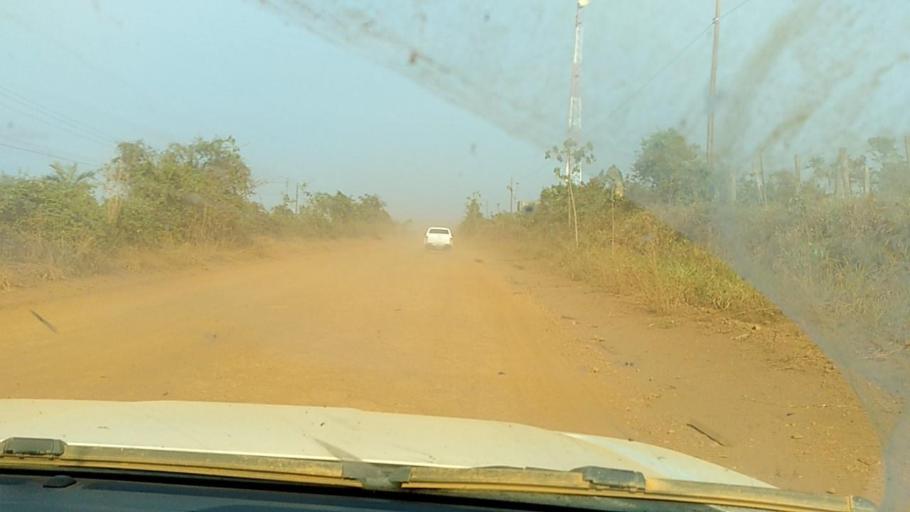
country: BR
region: Rondonia
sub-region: Porto Velho
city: Porto Velho
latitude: -8.7598
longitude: -63.9715
